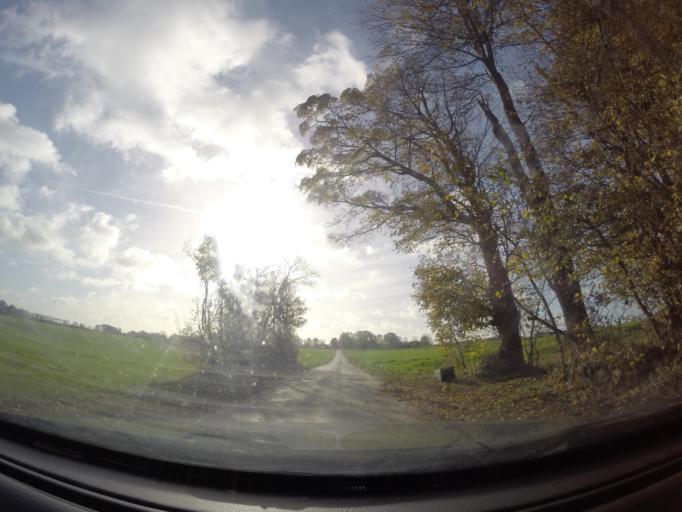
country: DK
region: South Denmark
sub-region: Faaborg-Midtfyn Kommune
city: Ringe
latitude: 55.2097
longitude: 10.5608
